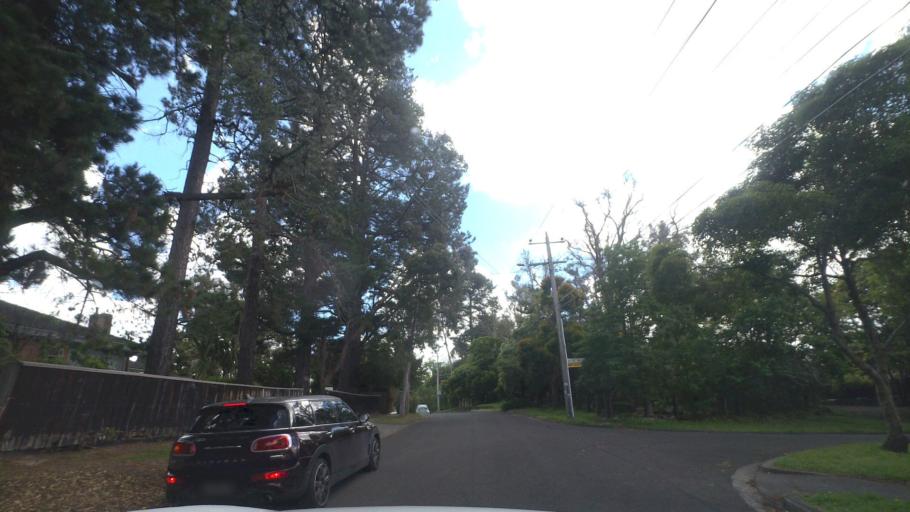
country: AU
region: Victoria
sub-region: Maroondah
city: Croydon South
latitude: -37.8114
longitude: 145.2631
